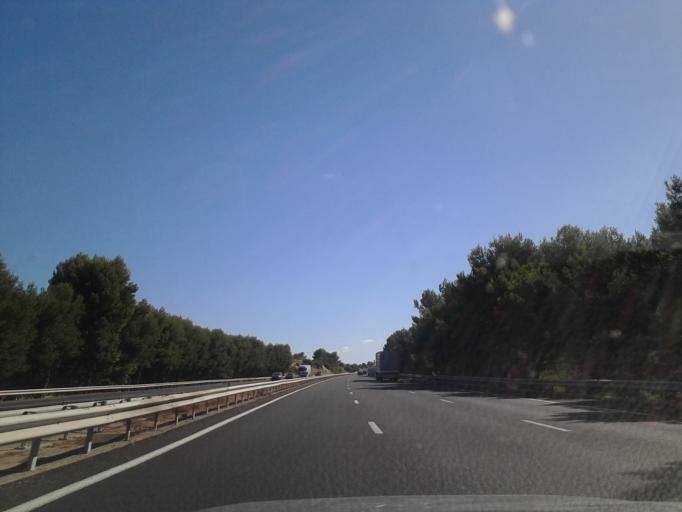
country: FR
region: Languedoc-Roussillon
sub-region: Departement de l'Herault
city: Vendres
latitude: 43.2961
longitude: 3.2001
